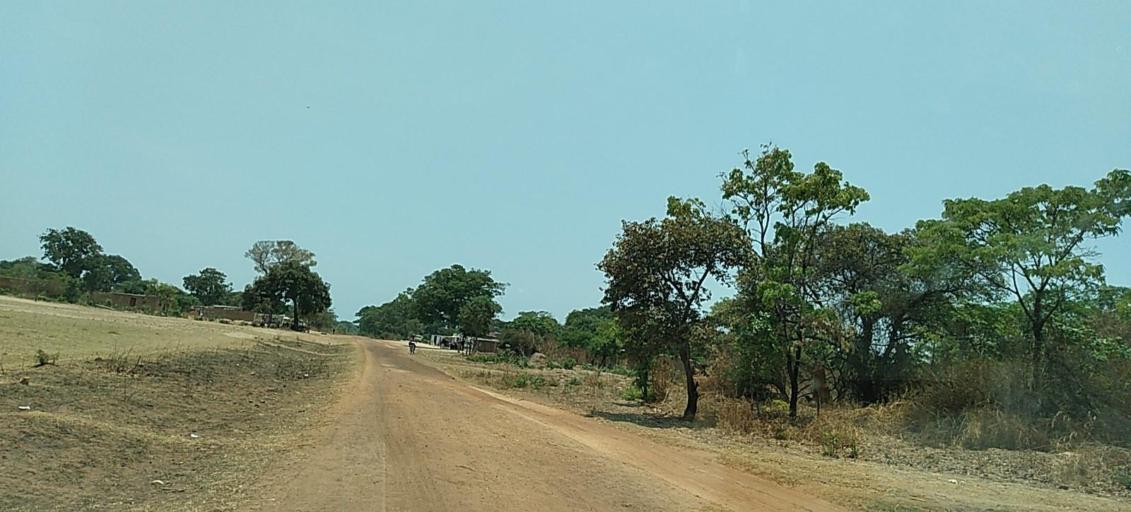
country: ZM
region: Copperbelt
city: Mpongwe
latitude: -13.7912
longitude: 27.8631
